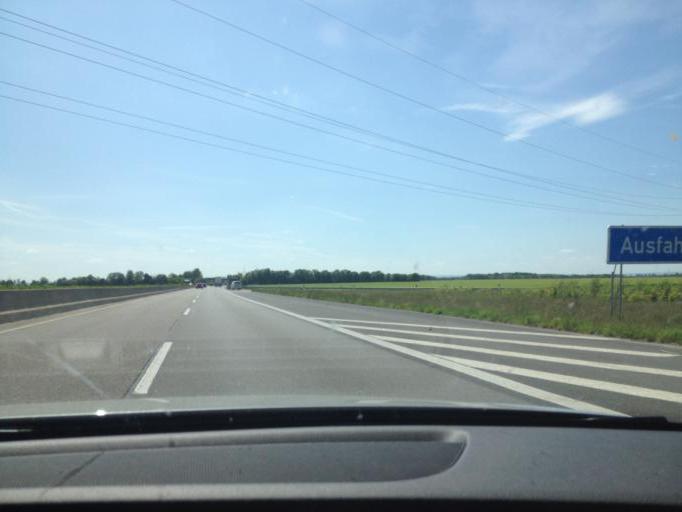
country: DE
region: North Rhine-Westphalia
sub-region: Regierungsbezirk Koln
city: Weilerswist
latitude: 50.7513
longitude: 6.8109
